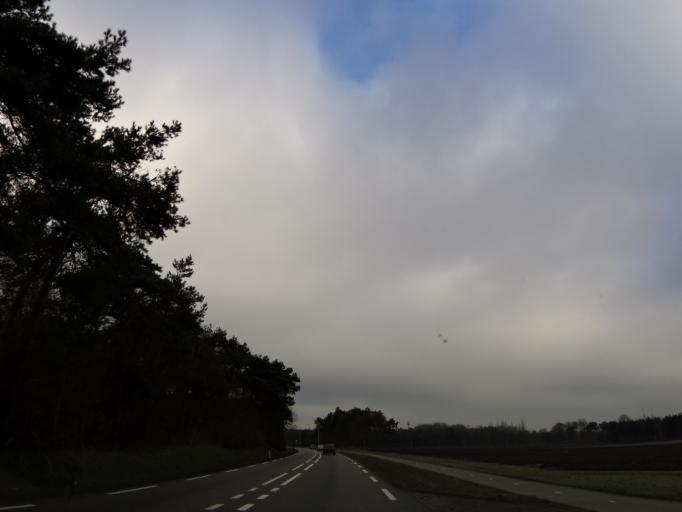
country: NL
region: Limburg
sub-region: Gemeente Peel en Maas
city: Maasbree
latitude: 51.3709
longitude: 5.9809
